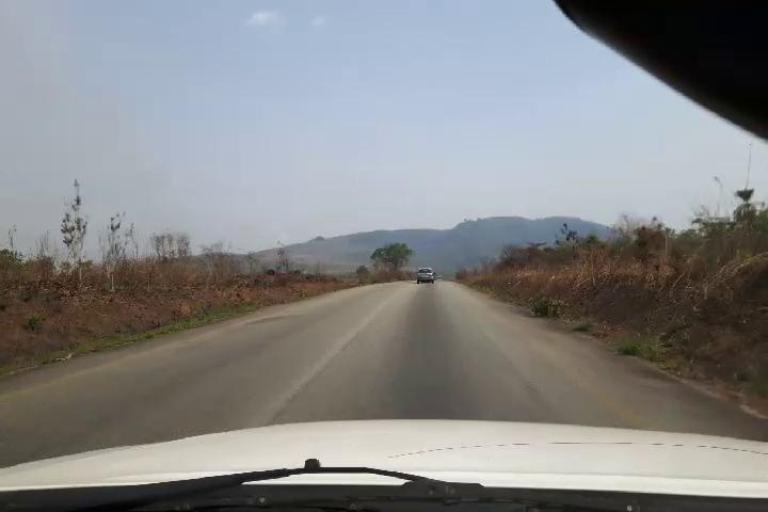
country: SL
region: Northern Province
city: Yonibana
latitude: 8.3903
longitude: -12.1914
